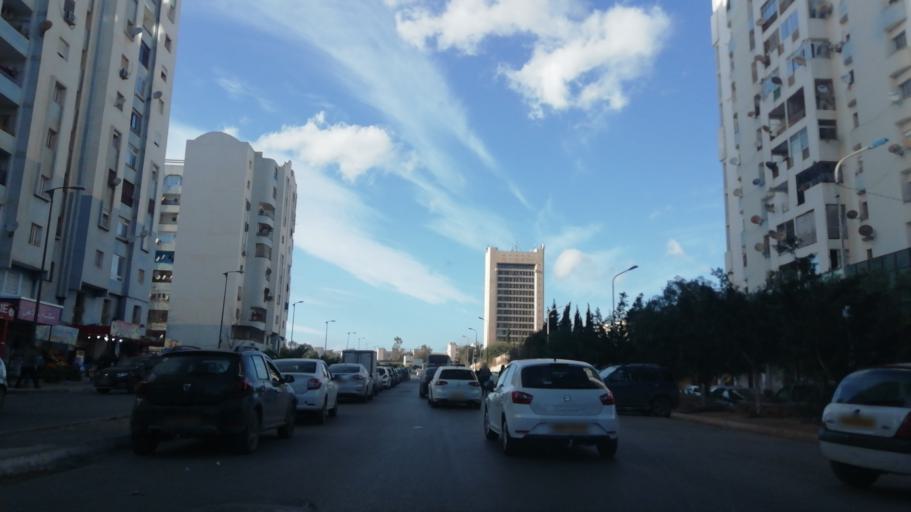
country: DZ
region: Oran
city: Bir el Djir
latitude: 35.7016
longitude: -0.5757
